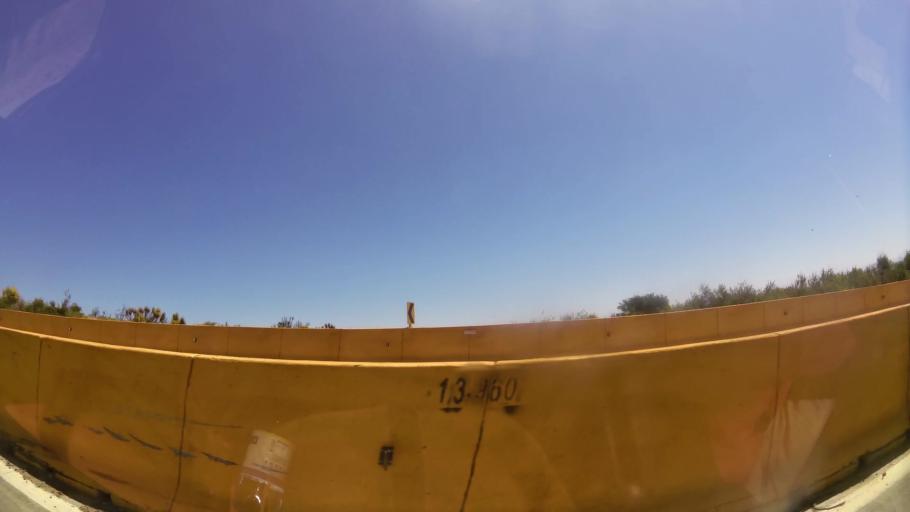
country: CL
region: Valparaiso
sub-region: Provincia de Valparaiso
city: Valparaiso
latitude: -33.0515
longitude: -71.6567
